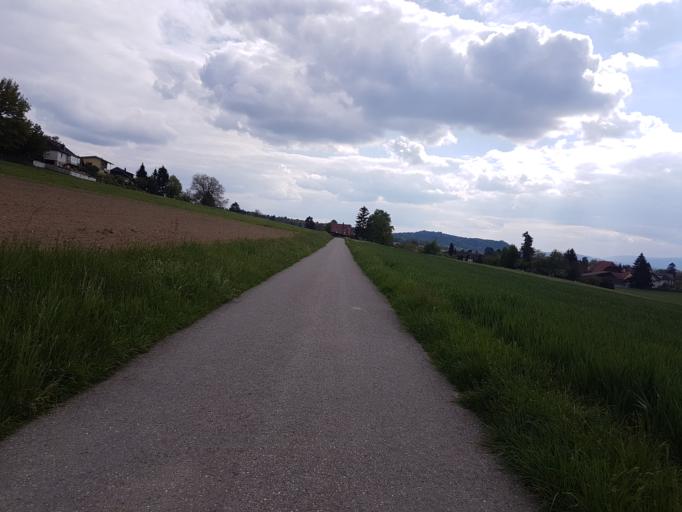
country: CH
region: Bern
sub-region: Seeland District
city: Arch
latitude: 47.1547
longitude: 7.4116
